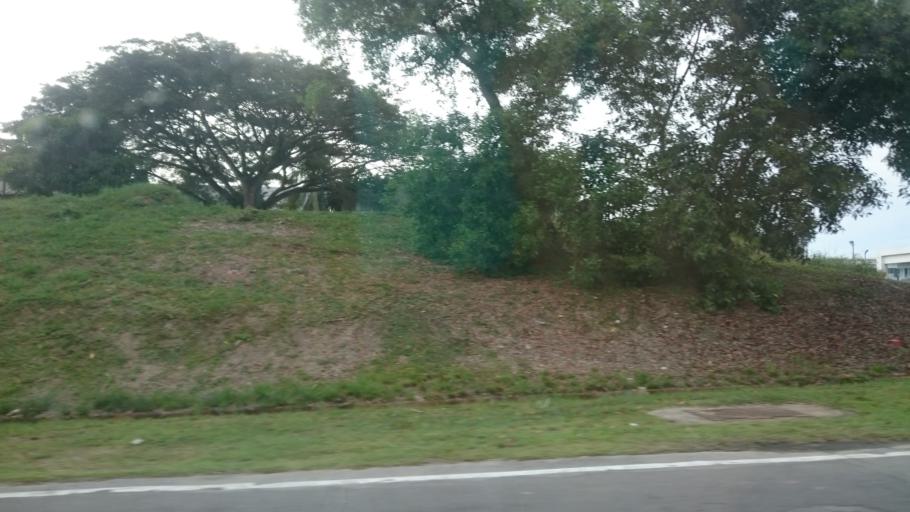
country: BN
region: Brunei and Muara
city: Bandar Seri Begawan
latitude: 4.8935
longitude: 114.9107
